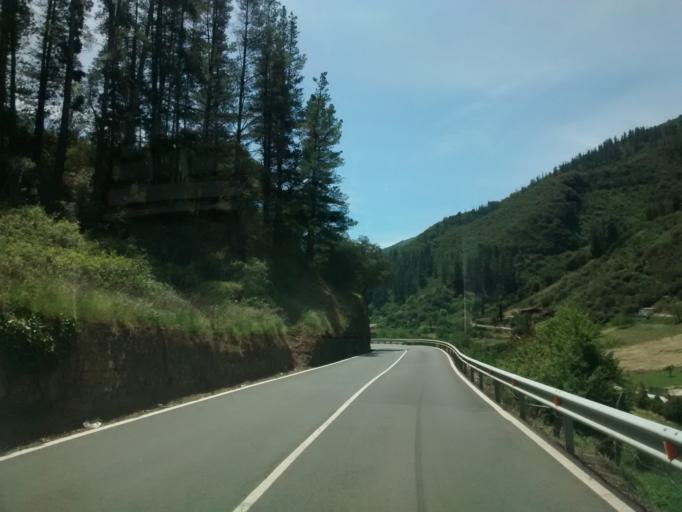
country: ES
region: Cantabria
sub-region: Provincia de Cantabria
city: Potes
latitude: 43.1478
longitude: -4.6268
